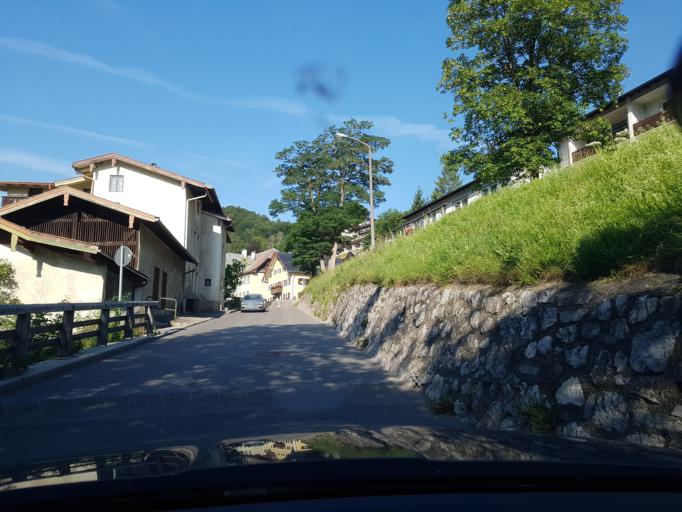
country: DE
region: Bavaria
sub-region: Upper Bavaria
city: Berchtesgaden
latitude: 47.6390
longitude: 13.0112
